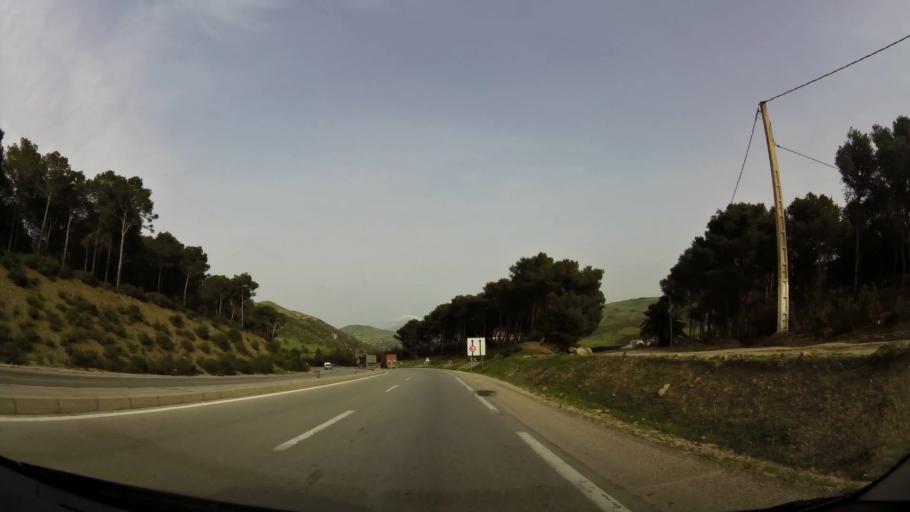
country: MA
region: Tanger-Tetouan
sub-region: Tetouan
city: Saddina
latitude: 35.5497
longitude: -5.5482
